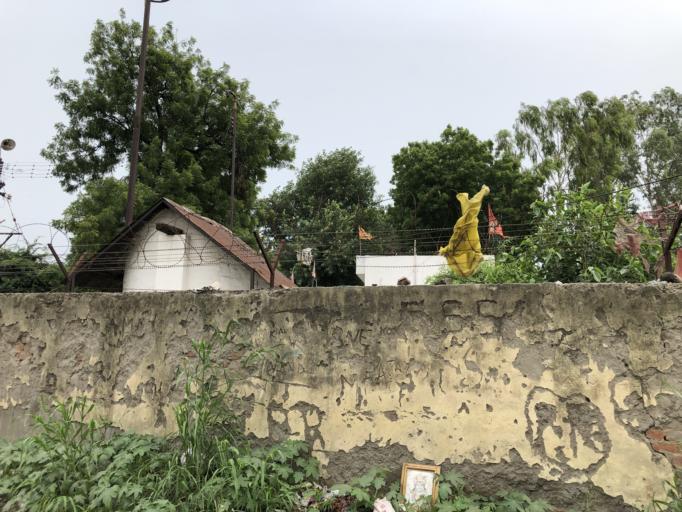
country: IN
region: NCT
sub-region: New Delhi
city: New Delhi
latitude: 28.5787
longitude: 77.2466
